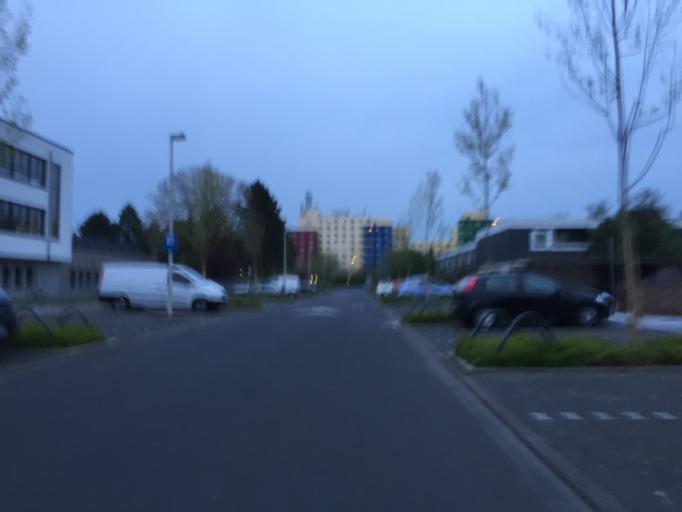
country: DE
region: North Rhine-Westphalia
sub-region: Regierungsbezirk Koln
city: Alfter
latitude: 50.7503
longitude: 7.0402
